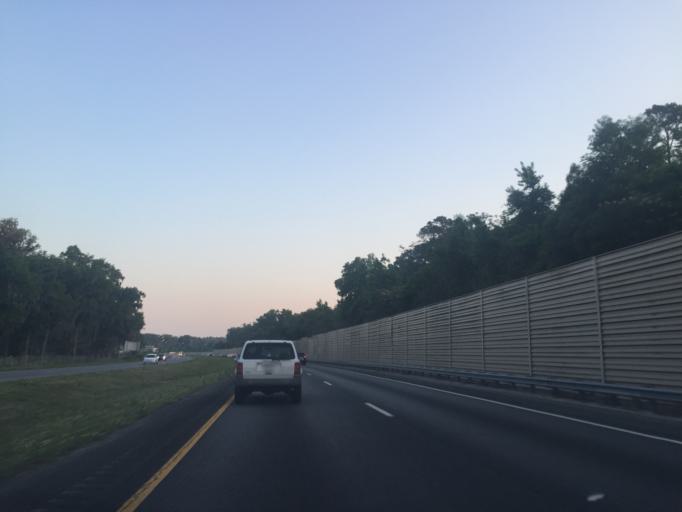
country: US
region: Georgia
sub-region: Chatham County
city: Thunderbolt
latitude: 32.0140
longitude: -81.0838
